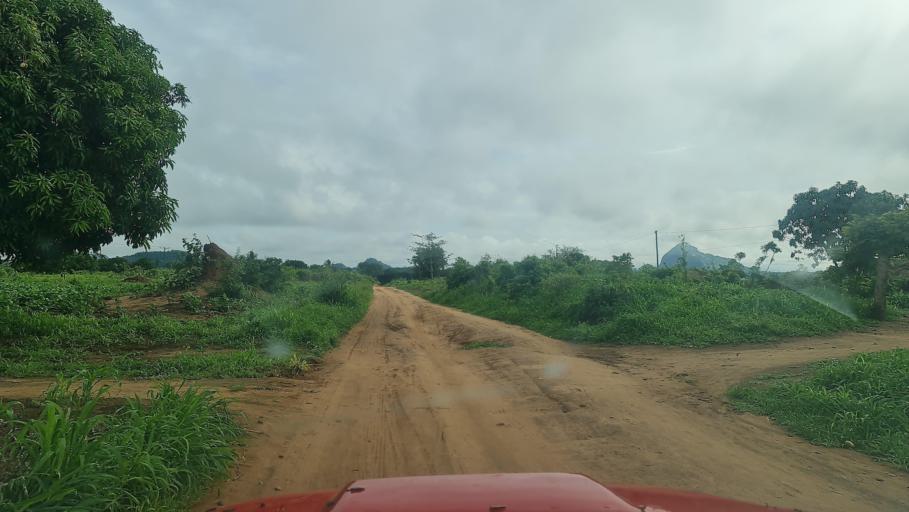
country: MW
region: Southern Region
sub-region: Nsanje District
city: Nsanje
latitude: -17.2822
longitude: 35.6137
